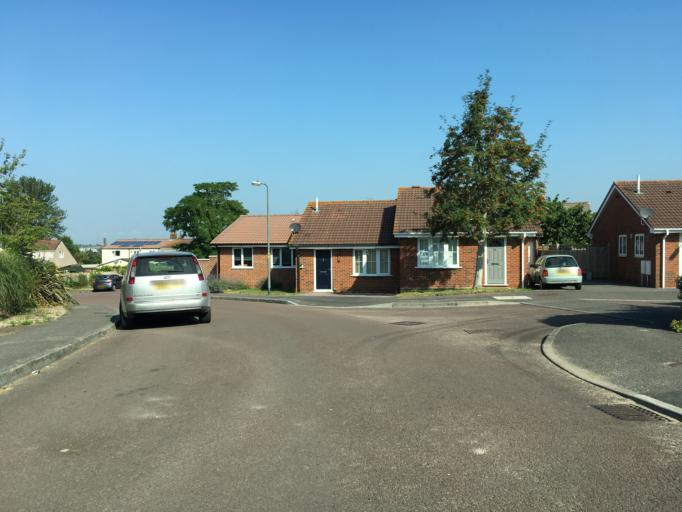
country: GB
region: England
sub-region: South Gloucestershire
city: Stoke Gifford
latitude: 51.5164
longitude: -2.5383
